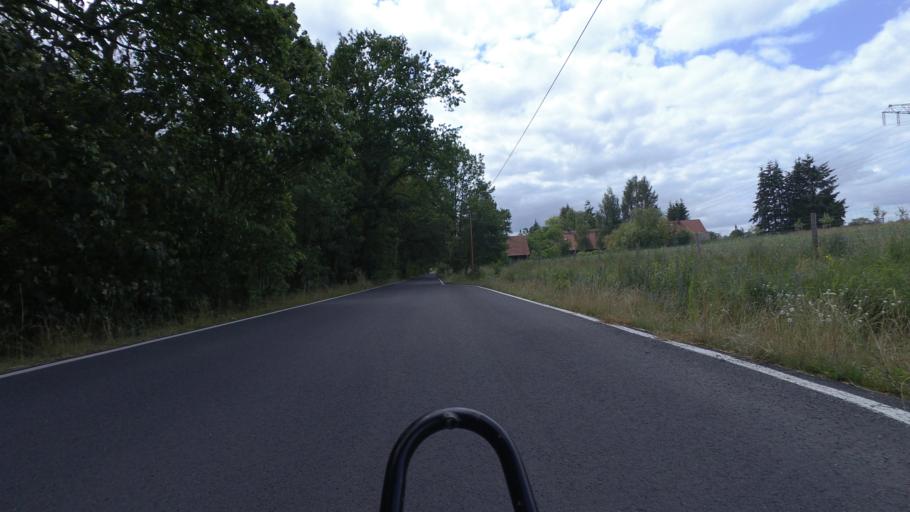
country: DE
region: Brandenburg
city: Ludwigsfelde
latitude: 52.2479
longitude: 13.2933
